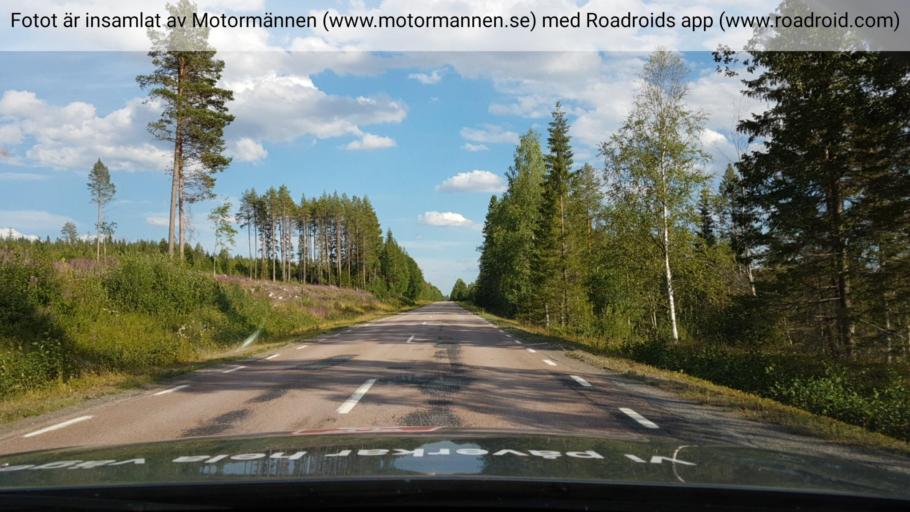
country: SE
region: Jaemtland
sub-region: Stroemsunds Kommun
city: Stroemsund
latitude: 63.6903
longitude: 15.9003
